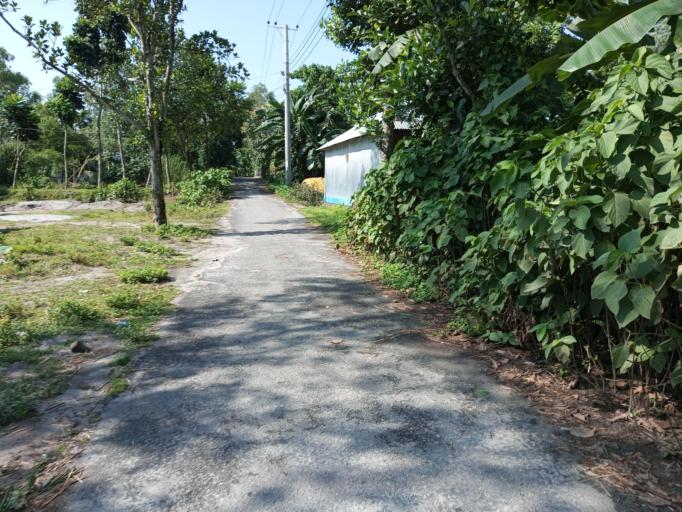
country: BD
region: Rangpur Division
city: Lalmanirhat
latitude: 25.9632
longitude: 89.2666
